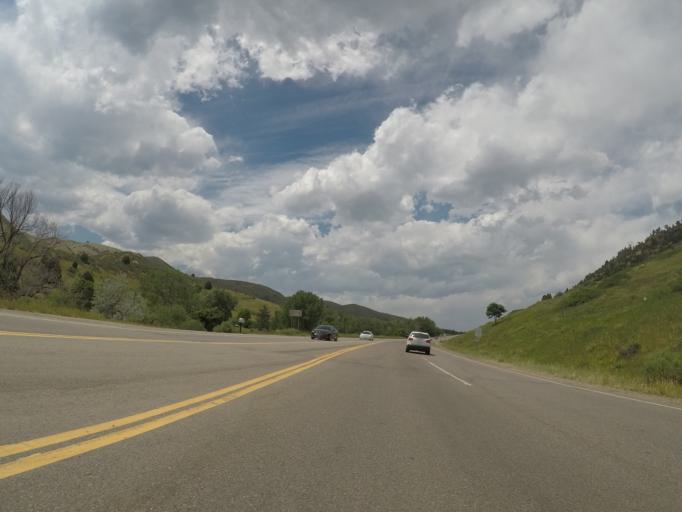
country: US
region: Colorado
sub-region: Jefferson County
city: West Pleasant View
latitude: 39.6809
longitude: -105.1978
